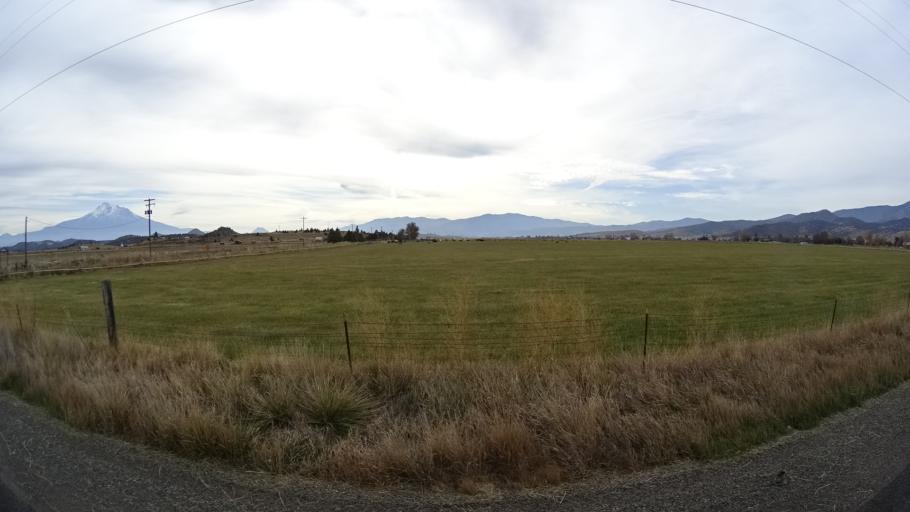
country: US
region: California
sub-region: Siskiyou County
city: Montague
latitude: 41.6471
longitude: -122.5140
